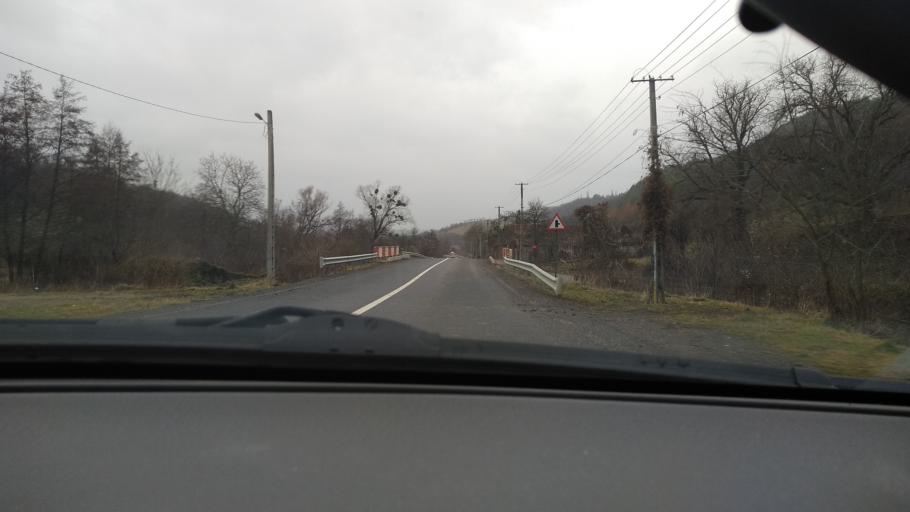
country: RO
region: Mures
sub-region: Comuna Magherani
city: Magherani
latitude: 46.5779
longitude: 24.9332
